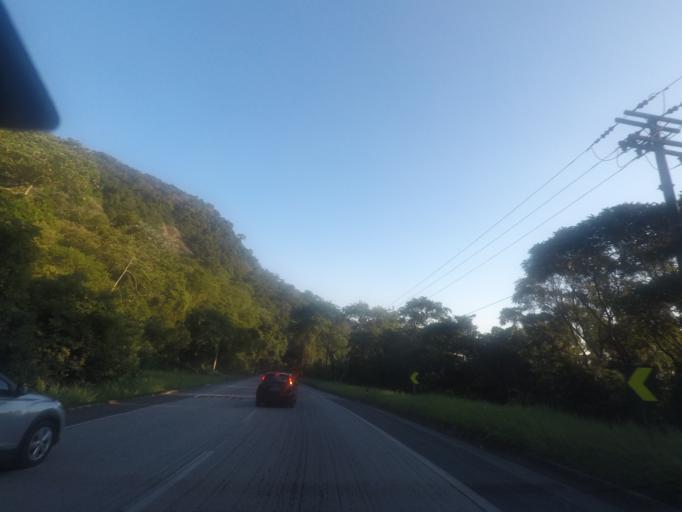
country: BR
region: Rio de Janeiro
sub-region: Petropolis
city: Petropolis
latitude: -22.5348
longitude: -43.2335
